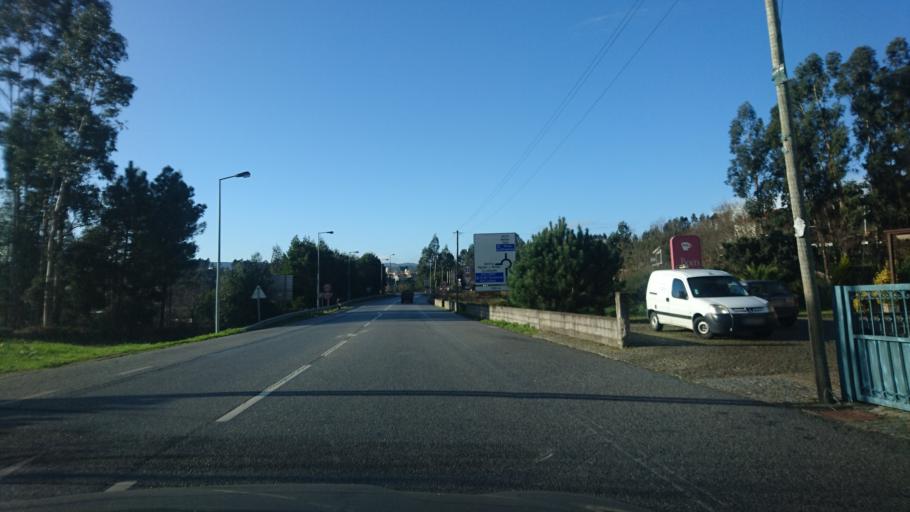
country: PT
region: Porto
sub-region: Paredes
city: Recarei
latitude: 41.1484
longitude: -8.3926
